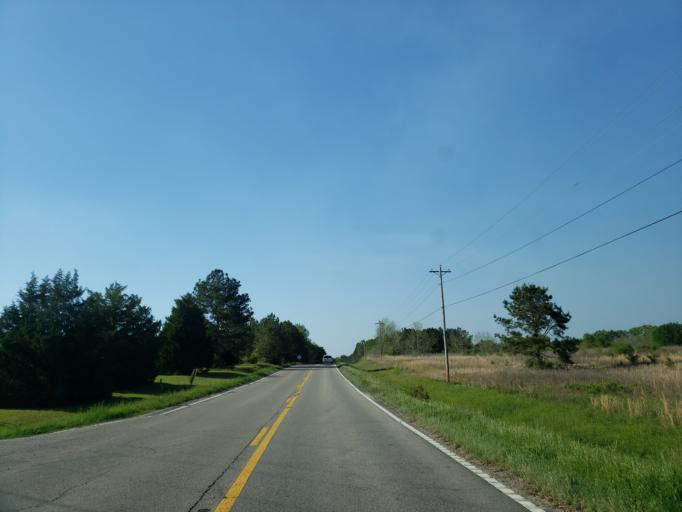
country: US
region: Mississippi
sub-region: Perry County
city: Richton
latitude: 31.4336
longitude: -88.9655
